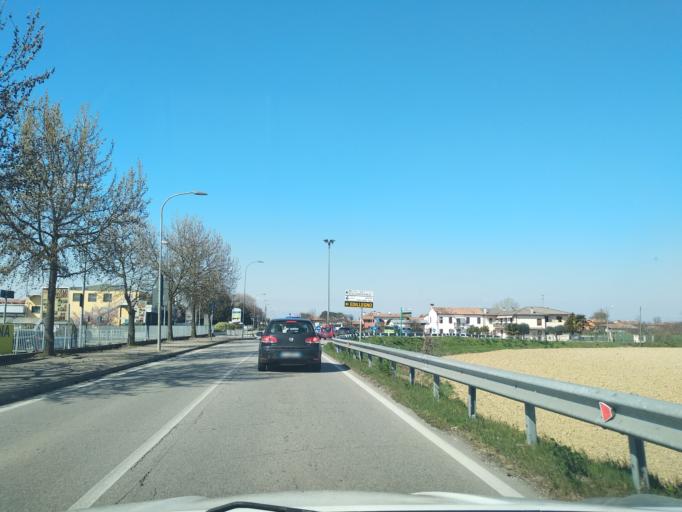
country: IT
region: Veneto
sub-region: Provincia di Padova
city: Taggi
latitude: 45.4585
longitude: 11.8230
